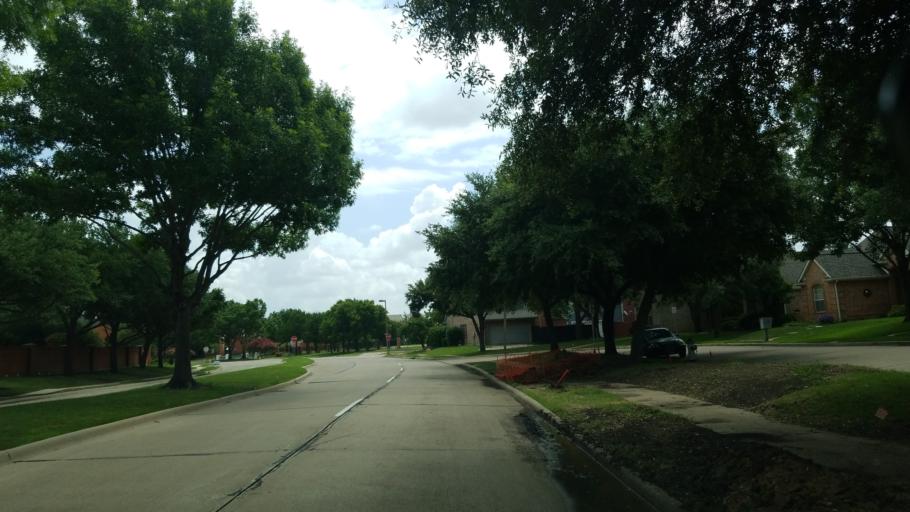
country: US
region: Texas
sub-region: Dallas County
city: Coppell
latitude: 32.9389
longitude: -96.9583
